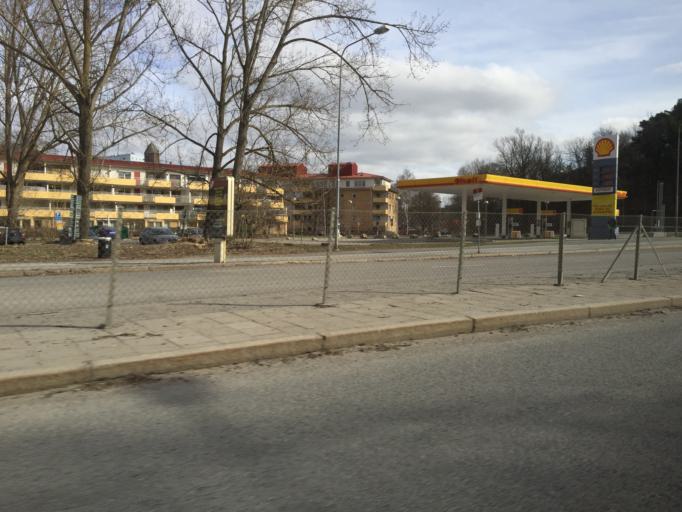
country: SE
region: Stockholm
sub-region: Solna Kommun
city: Solna
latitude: 59.3578
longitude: 18.0072
